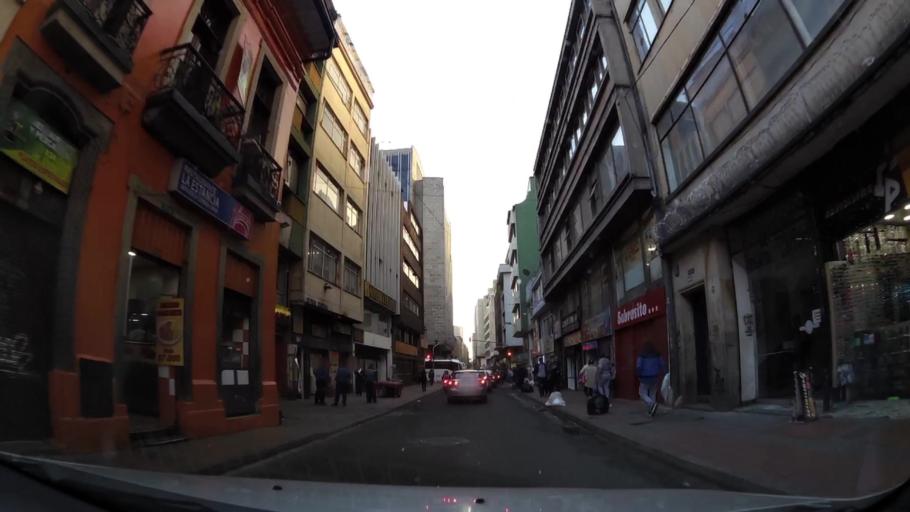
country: CO
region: Bogota D.C.
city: Bogota
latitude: 4.6046
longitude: -74.0729
